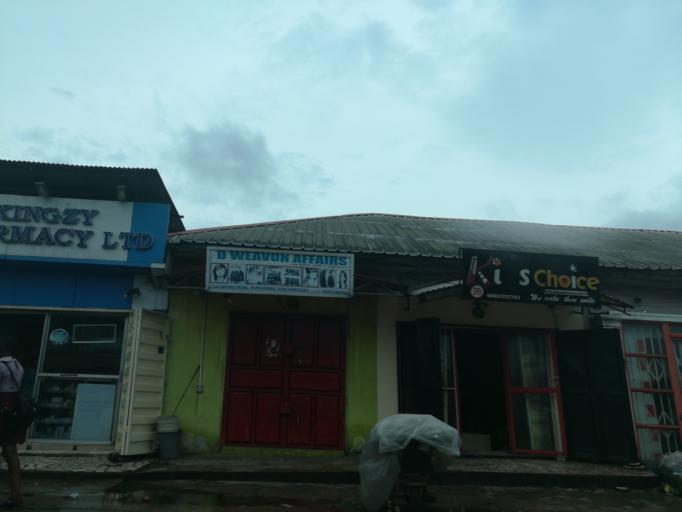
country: NG
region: Rivers
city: Port Harcourt
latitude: 4.8542
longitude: 7.0322
